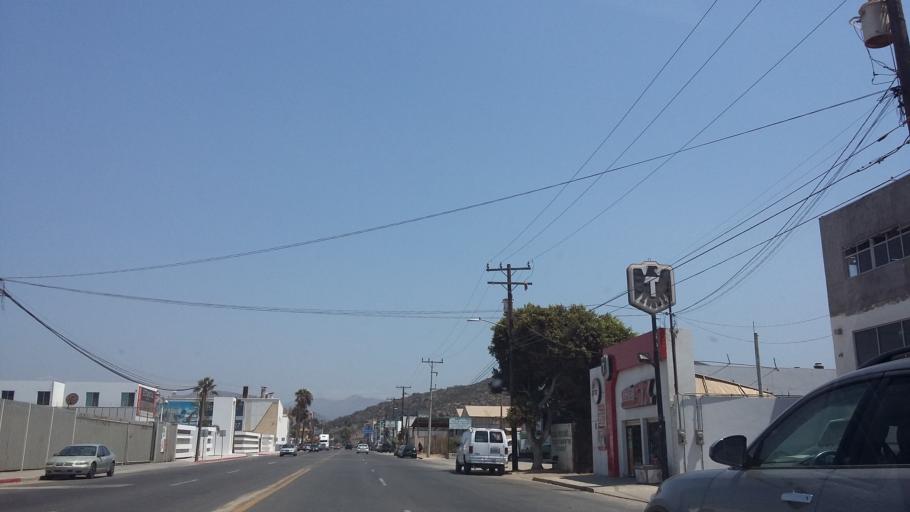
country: MX
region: Baja California
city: Ensenada
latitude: 31.8412
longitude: -116.6071
